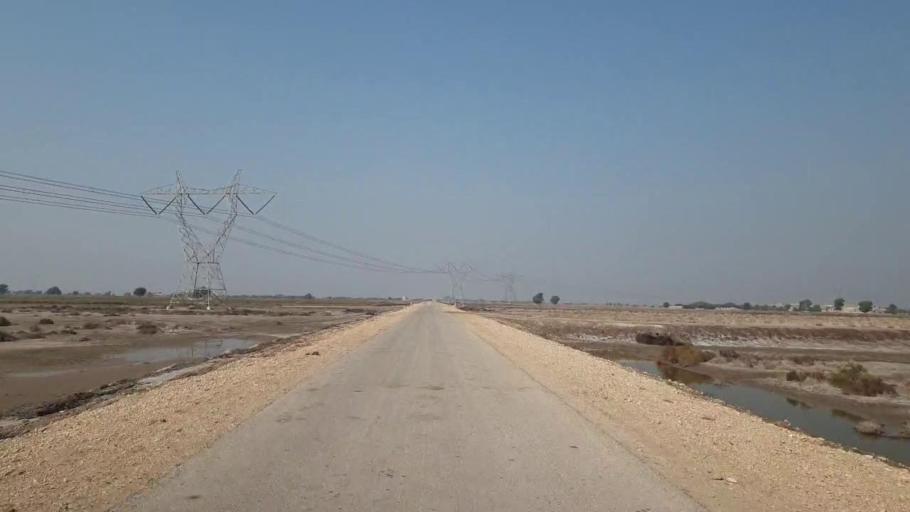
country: PK
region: Sindh
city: Sehwan
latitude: 26.4276
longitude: 67.7711
